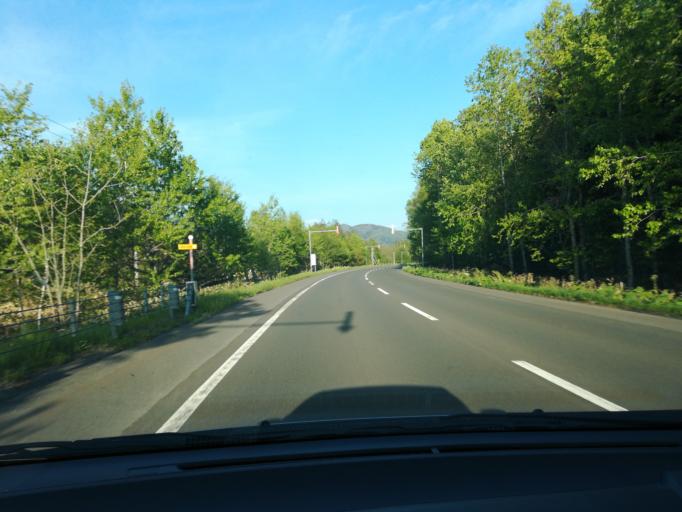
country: JP
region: Hokkaido
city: Shimo-furano
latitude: 43.1352
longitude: 142.6444
